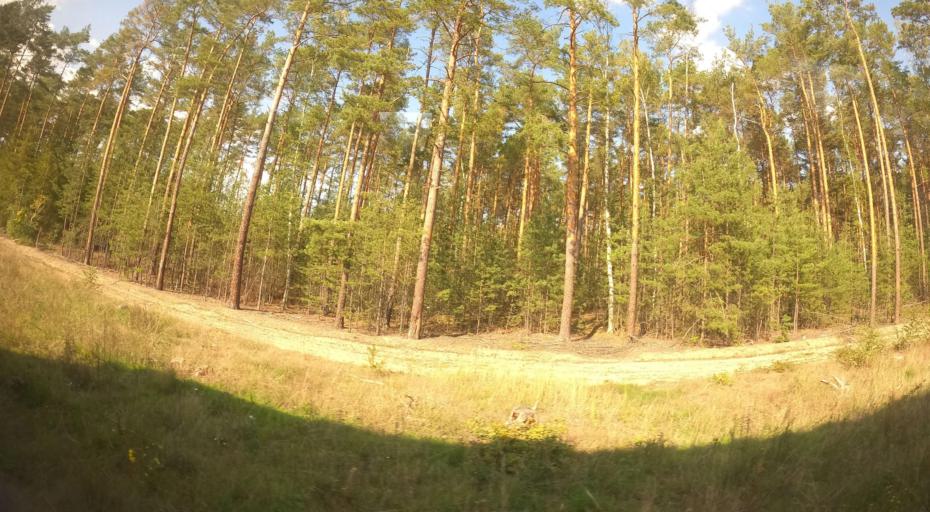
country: PL
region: Lubusz
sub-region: Powiat zielonogorski
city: Swidnica
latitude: 51.9150
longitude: 15.3470
